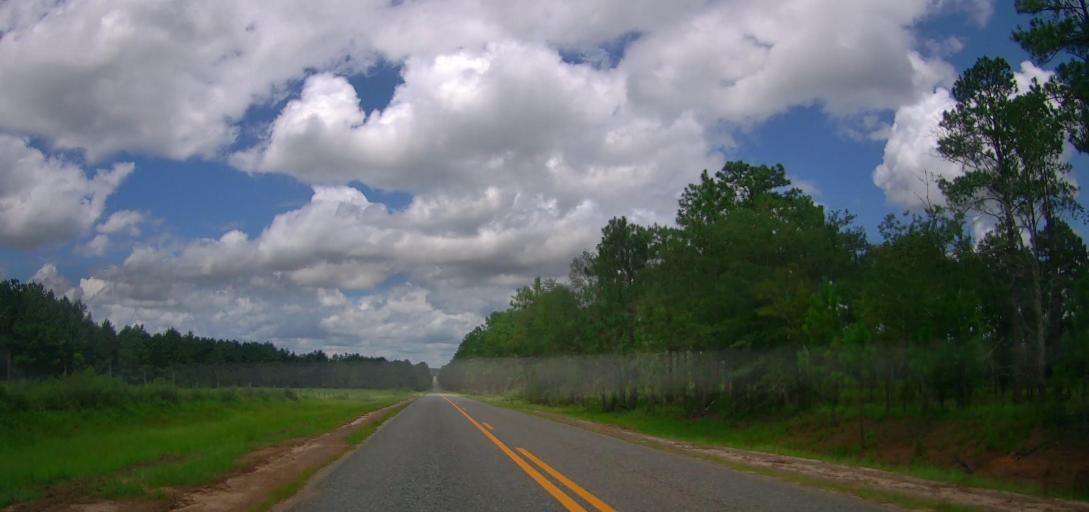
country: US
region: Georgia
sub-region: Turner County
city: Ashburn
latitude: 31.7122
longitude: -83.5055
